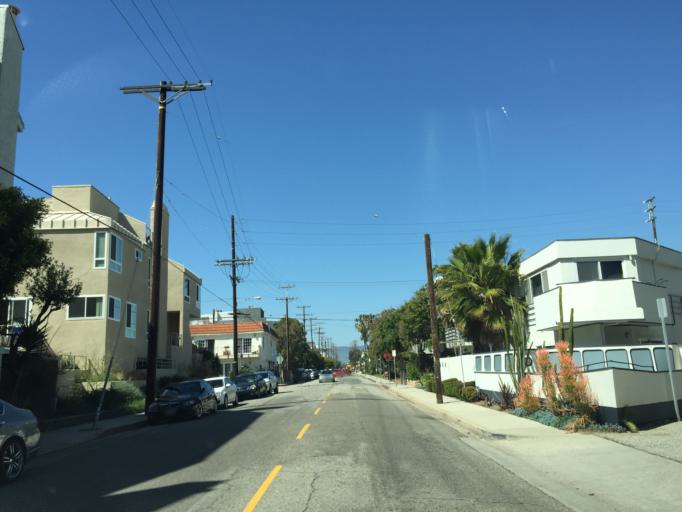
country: US
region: California
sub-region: Los Angeles County
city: Marina del Rey
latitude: 33.9749
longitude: -118.4619
